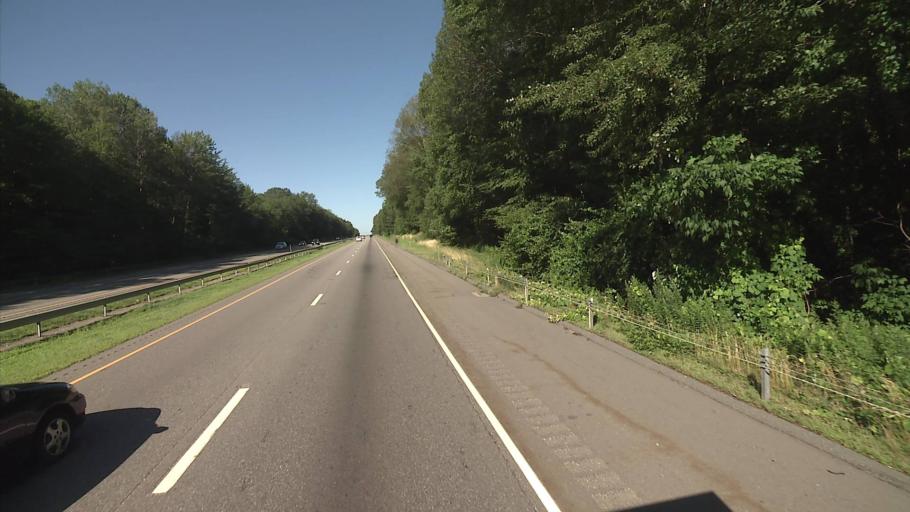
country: US
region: Connecticut
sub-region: New London County
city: Baltic
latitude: 41.5766
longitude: -72.0787
